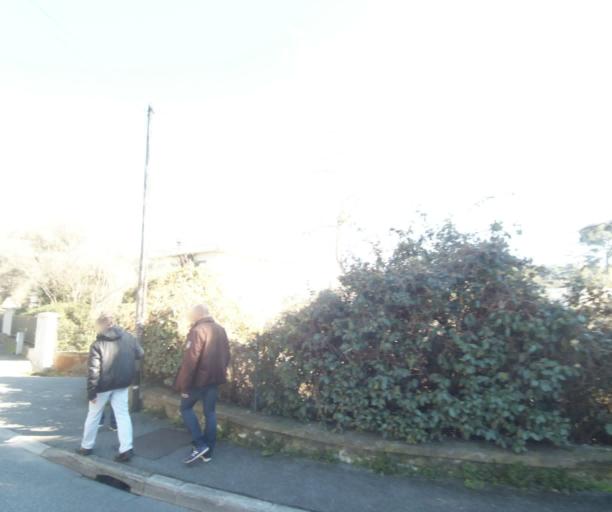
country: FR
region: Provence-Alpes-Cote d'Azur
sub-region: Departement des Alpes-Maritimes
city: Antibes
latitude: 43.5653
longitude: 7.1246
